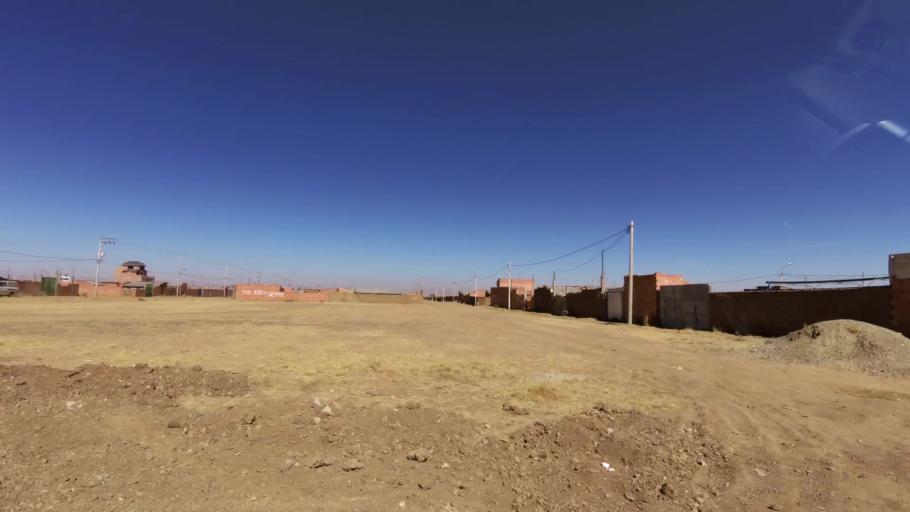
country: BO
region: La Paz
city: La Paz
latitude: -16.6141
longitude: -68.1955
